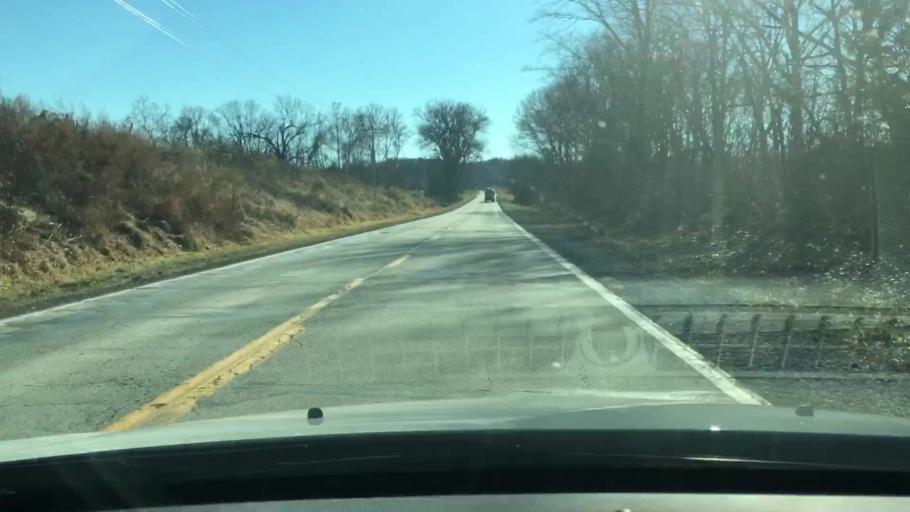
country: US
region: Illinois
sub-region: Morgan County
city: Meredosia
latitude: 39.7159
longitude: -90.5685
